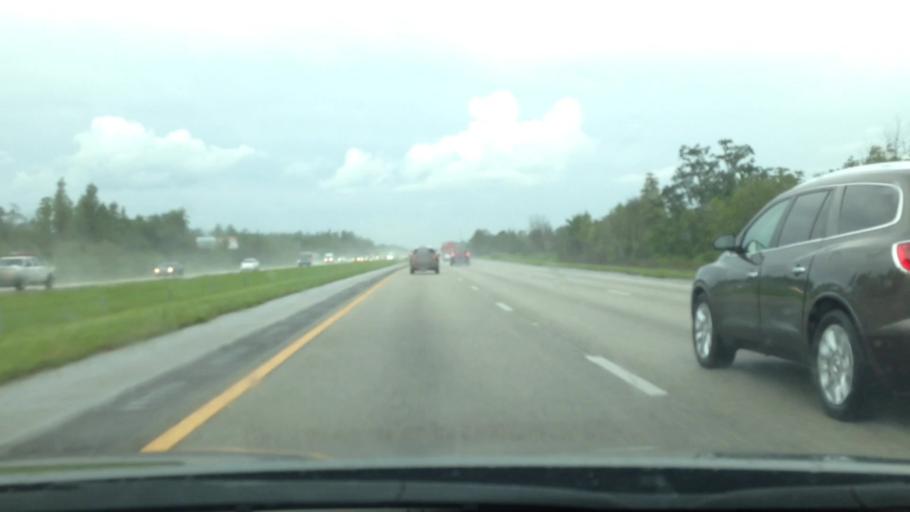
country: US
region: Florida
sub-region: Polk County
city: Lake Alfred
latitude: 28.1897
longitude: -81.7235
